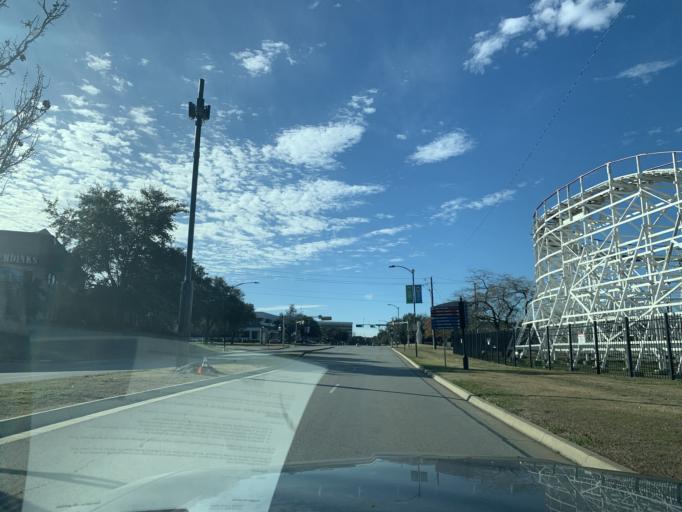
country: US
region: Texas
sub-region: Tarrant County
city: Arlington
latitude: 32.7535
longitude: -97.0676
